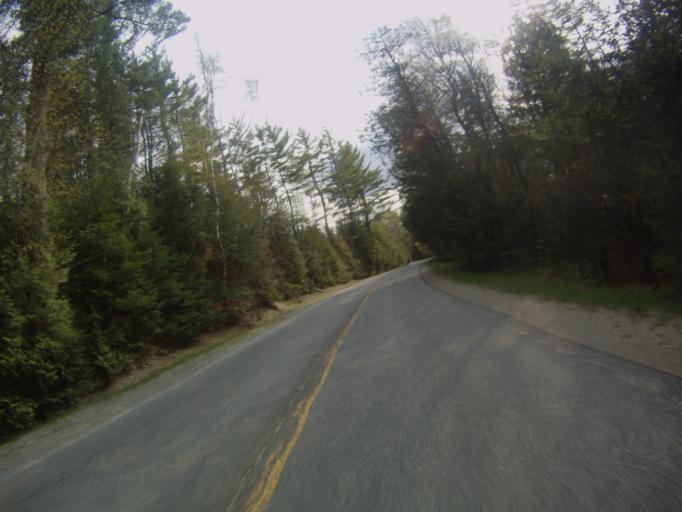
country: US
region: New York
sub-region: Warren County
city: Warrensburg
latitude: 43.8438
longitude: -73.8256
